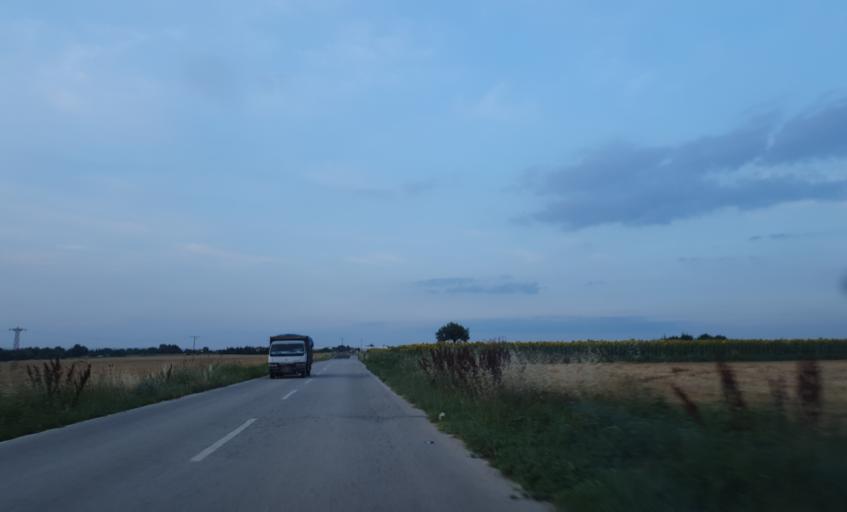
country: TR
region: Tekirdag
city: Beyazkoy
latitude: 41.4048
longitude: 27.6444
